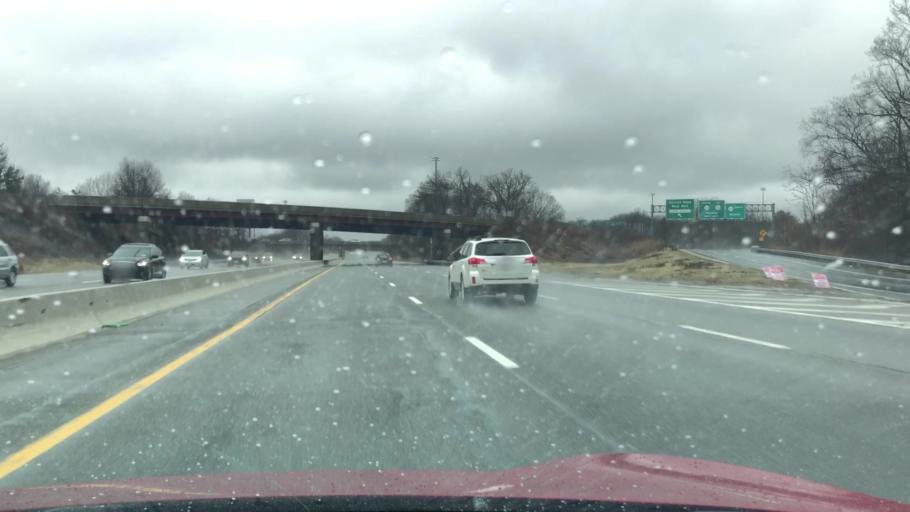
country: US
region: New Jersey
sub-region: Passaic County
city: Singac
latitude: 40.8979
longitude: -74.2484
